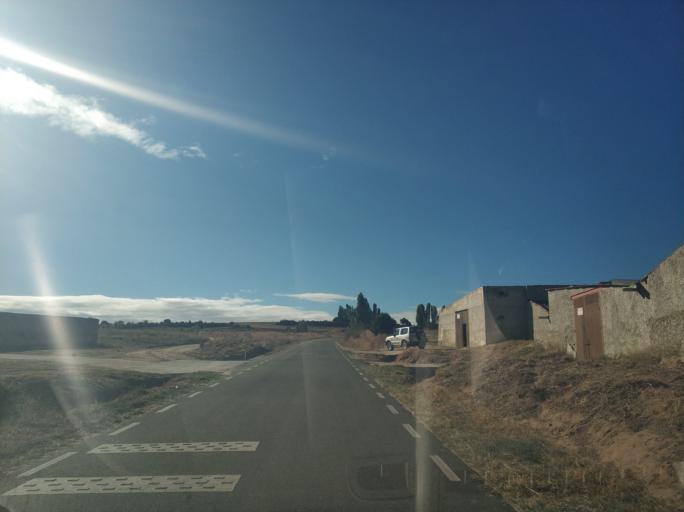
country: ES
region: Castille and Leon
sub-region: Provincia de Burgos
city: San Juan del Monte
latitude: 41.6798
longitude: -3.5242
